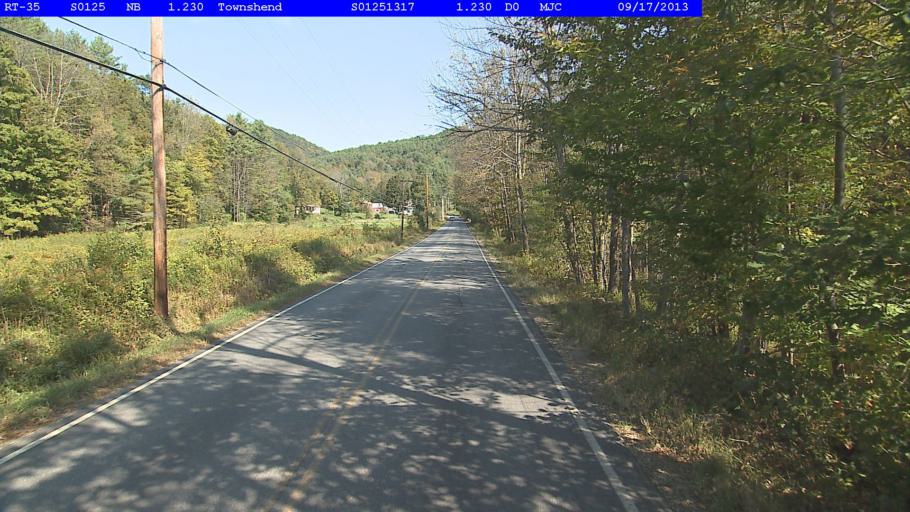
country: US
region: Vermont
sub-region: Windham County
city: Newfane
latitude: 43.0632
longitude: -72.6614
